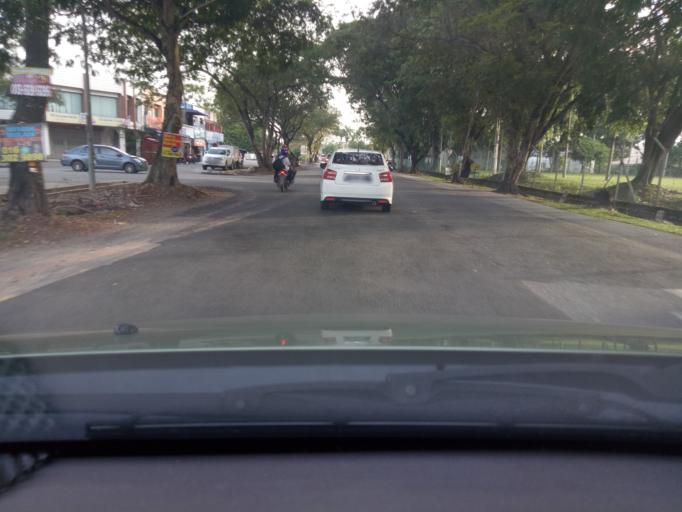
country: MY
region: Kedah
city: Alor Setar
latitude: 6.1281
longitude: 100.3492
